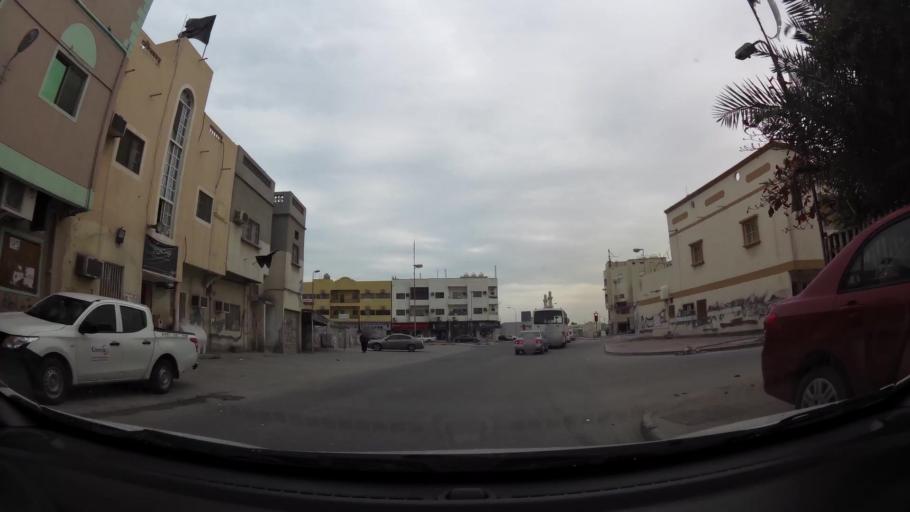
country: BH
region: Northern
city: Sitrah
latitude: 26.1657
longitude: 50.6083
